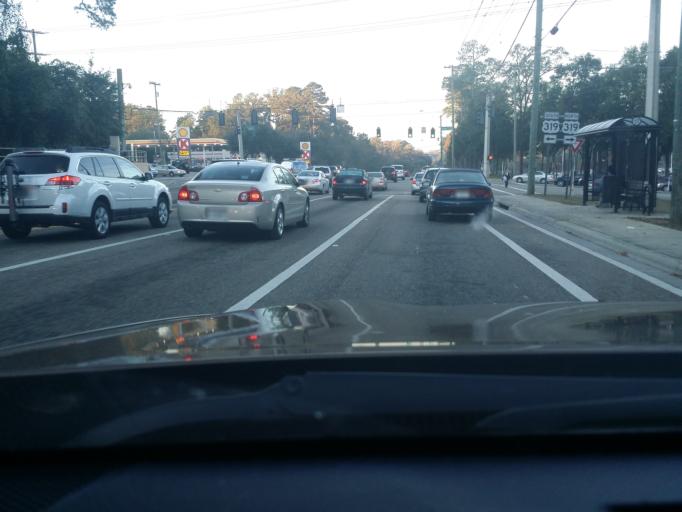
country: US
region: Florida
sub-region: Leon County
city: Tallahassee
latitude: 30.4701
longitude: -84.2303
